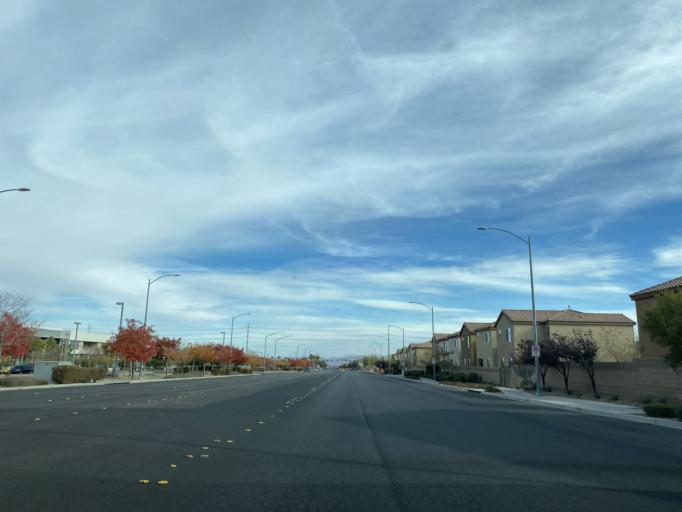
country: US
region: Nevada
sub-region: Clark County
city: Enterprise
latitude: 36.0411
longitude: -115.2483
